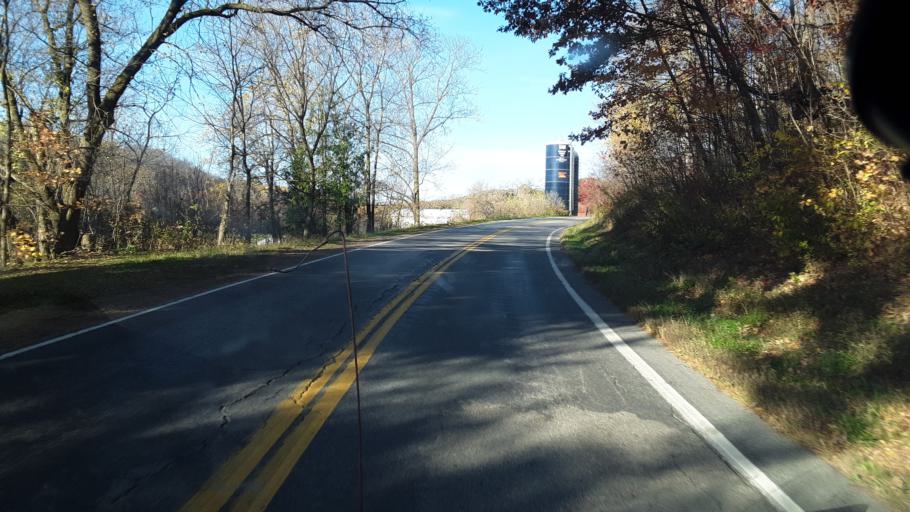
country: US
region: Wisconsin
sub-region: Vernon County
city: Hillsboro
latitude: 43.6607
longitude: -90.4324
